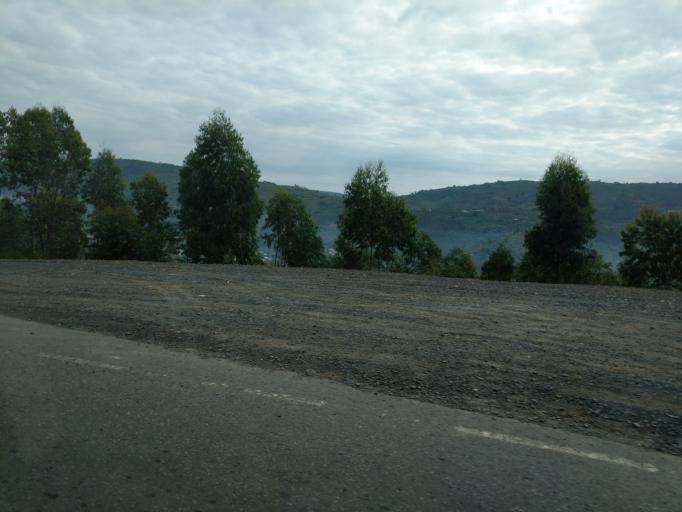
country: RW
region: Kigali
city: Kigali
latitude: -1.7785
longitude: 29.9279
